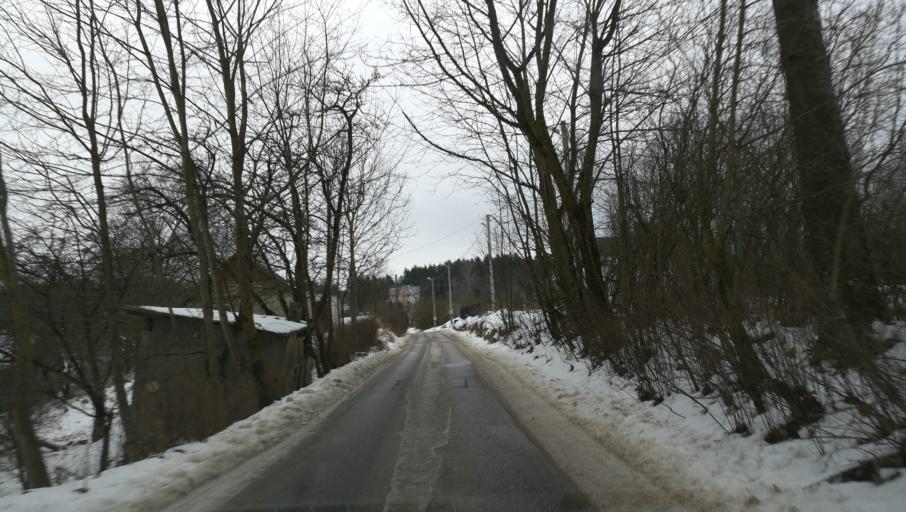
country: LT
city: Trakai
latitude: 54.6155
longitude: 24.9235
